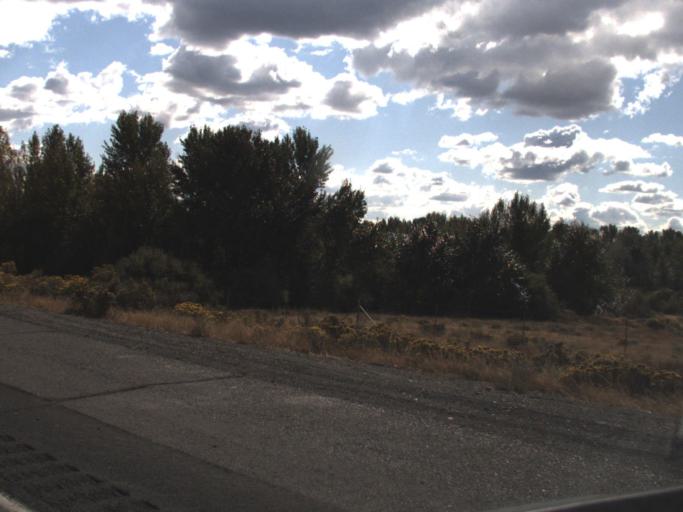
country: US
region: Washington
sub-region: Yakima County
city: Union Gap
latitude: 46.5223
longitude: -120.4695
